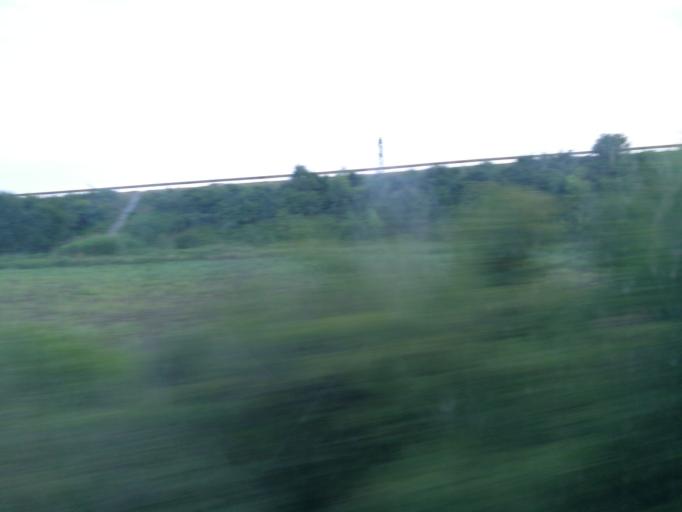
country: RO
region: Dambovita
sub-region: Comuna Racari
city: Mavrodin
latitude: 44.6467
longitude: 25.6999
